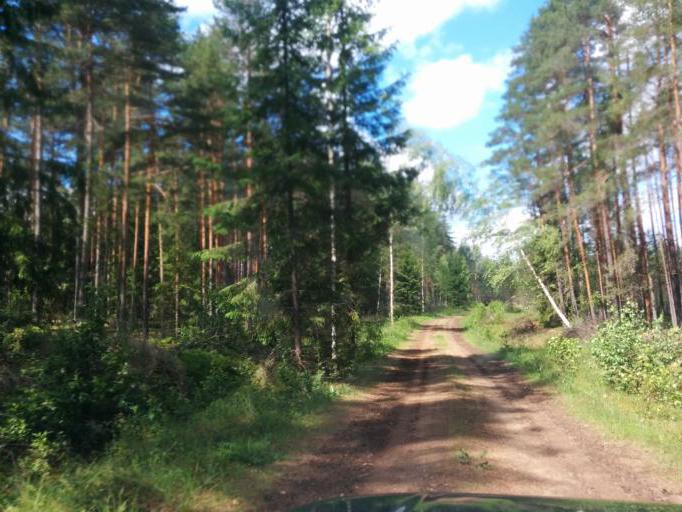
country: LV
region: Vilaka
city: Vilaka
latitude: 57.3331
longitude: 27.6820
